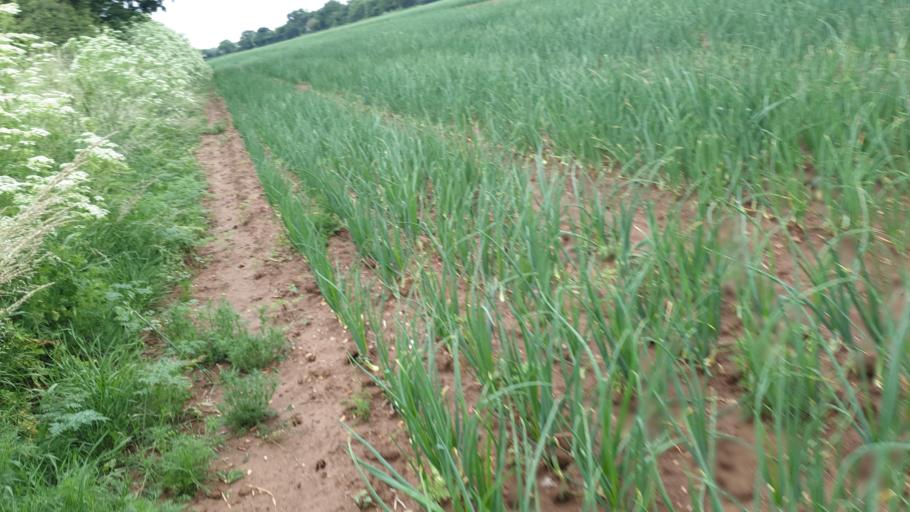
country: GB
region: England
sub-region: Essex
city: Alresford
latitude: 51.8622
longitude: 1.0315
